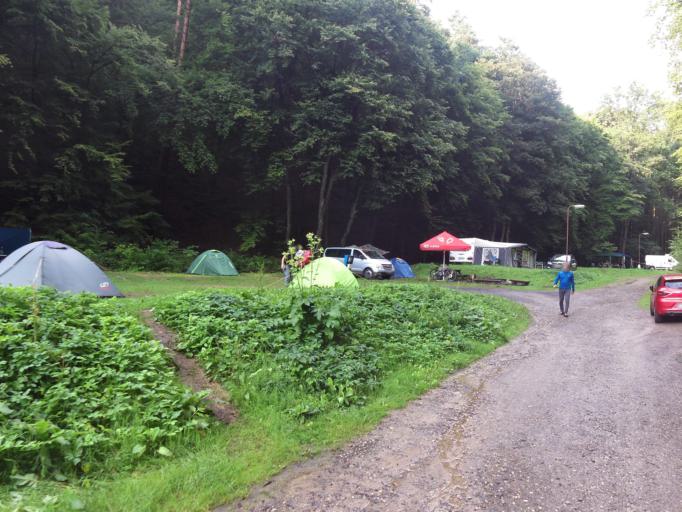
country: CZ
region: Central Bohemia
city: Mseno
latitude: 50.4383
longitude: 14.5876
